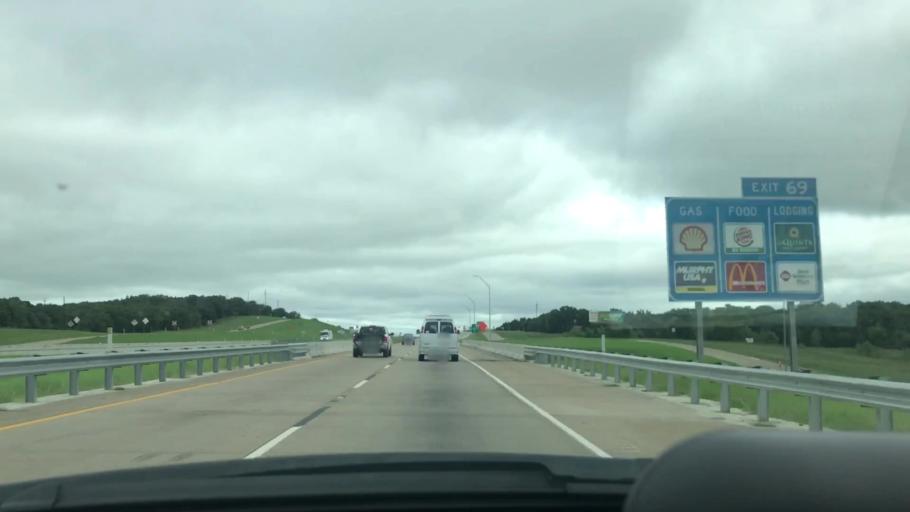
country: US
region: Texas
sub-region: Grayson County
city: Denison
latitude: 33.7485
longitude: -96.5843
